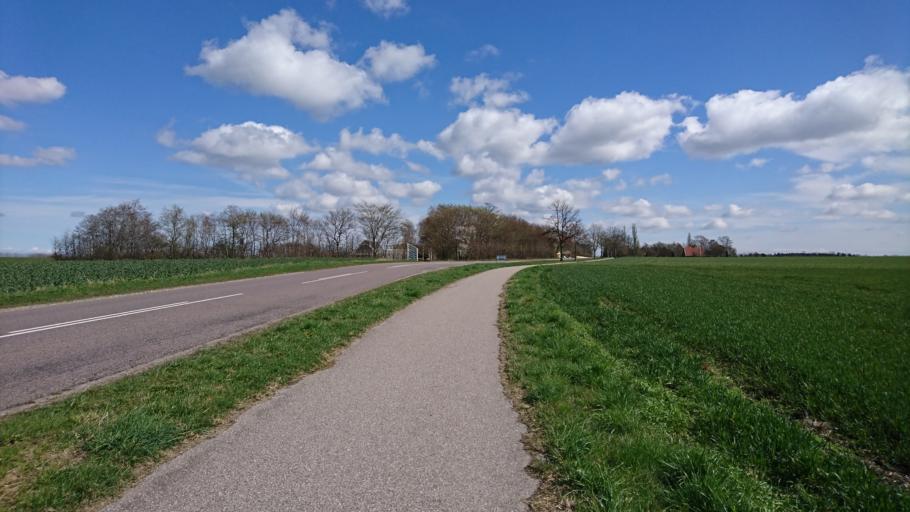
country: DK
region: Capital Region
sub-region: Egedal Kommune
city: Vekso
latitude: 55.7709
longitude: 12.2241
